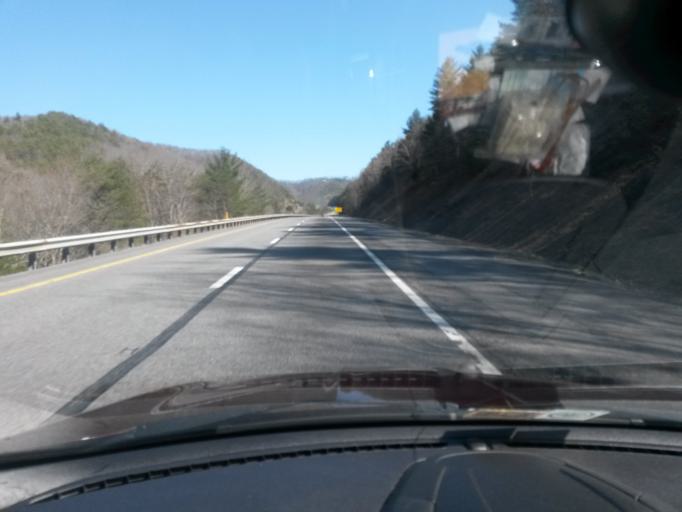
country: US
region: West Virginia
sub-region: Greenbrier County
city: White Sulphur Springs
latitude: 37.7871
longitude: -80.2482
